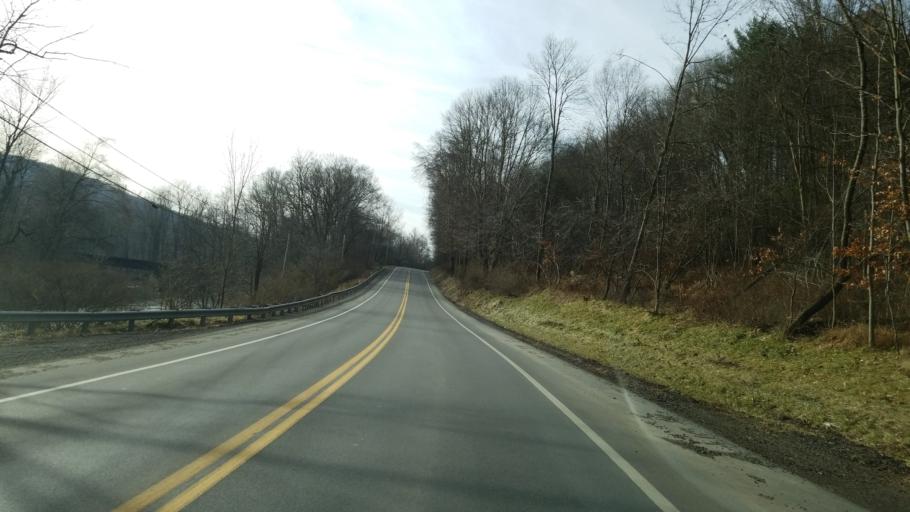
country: US
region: Pennsylvania
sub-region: Jefferson County
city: Albion
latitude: 40.9659
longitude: -78.9094
